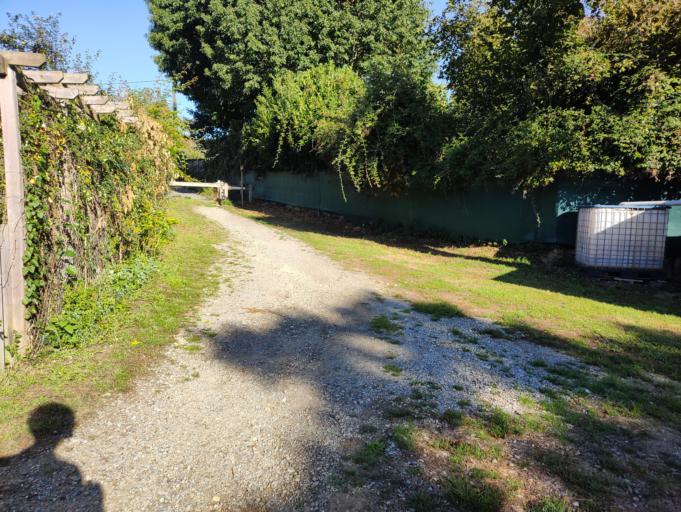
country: FR
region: Pays de la Loire
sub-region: Departement de la Loire-Atlantique
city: La Chapelle-sur-Erdre
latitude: 47.2567
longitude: -1.5632
